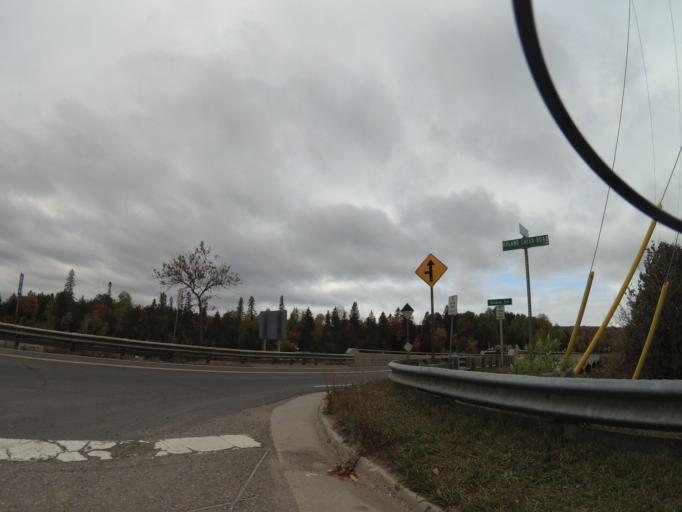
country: CA
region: Ontario
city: Renfrew
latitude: 45.2496
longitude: -77.1839
